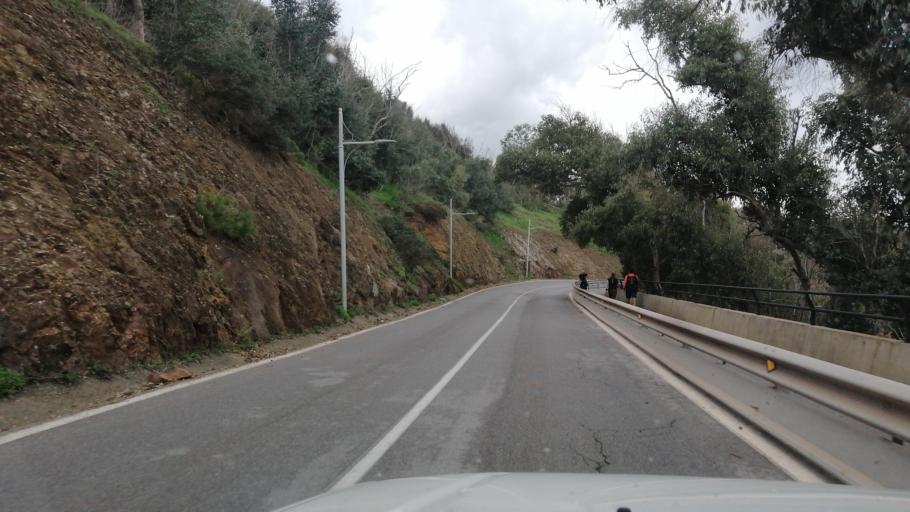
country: ES
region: Ceuta
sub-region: Ceuta
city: Ceuta
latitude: 35.9002
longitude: -5.2840
